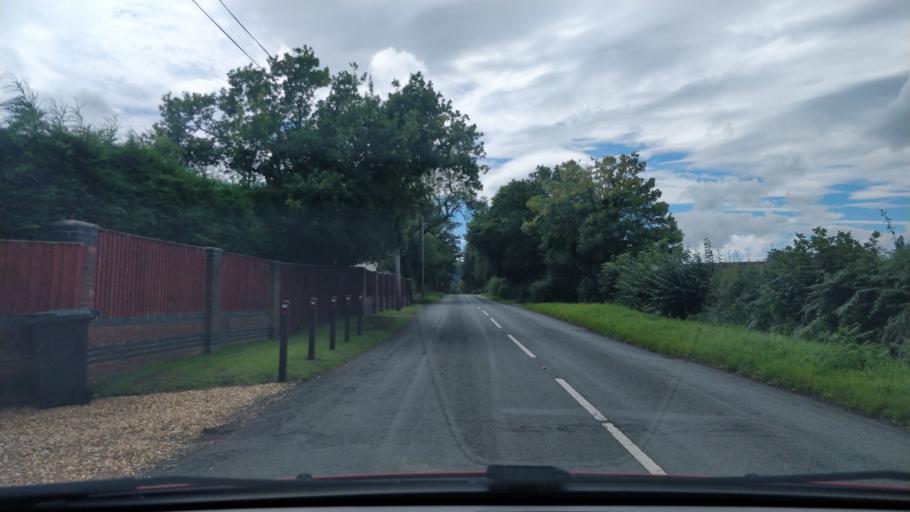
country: GB
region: Wales
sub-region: County of Flintshire
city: Hope
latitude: 53.1285
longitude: -3.0258
